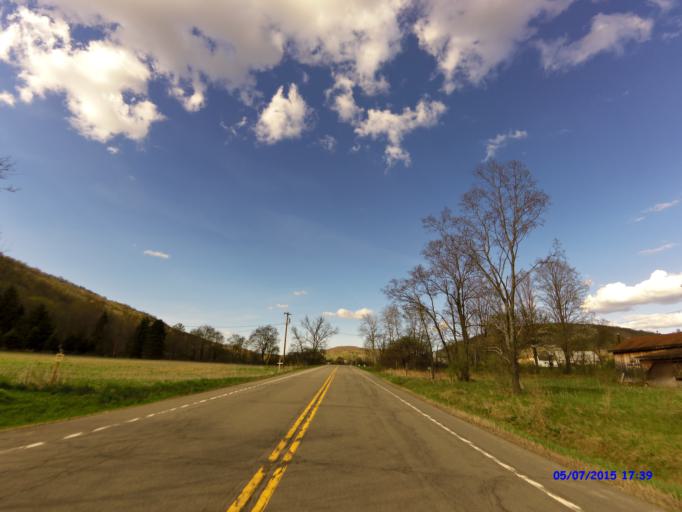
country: US
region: New York
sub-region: Cattaraugus County
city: Franklinville
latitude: 42.2648
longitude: -78.5452
